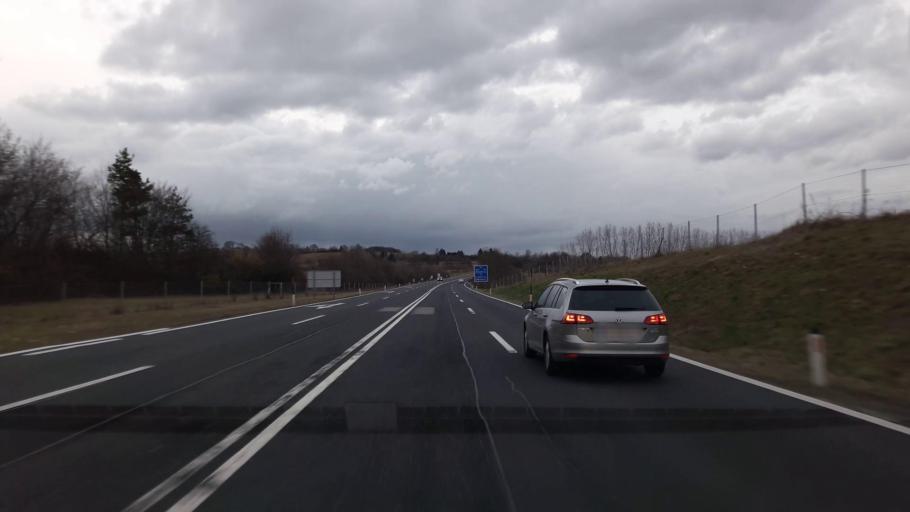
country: AT
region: Burgenland
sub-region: Politischer Bezirk Mattersburg
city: Mattersburg
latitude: 47.7245
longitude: 16.3773
